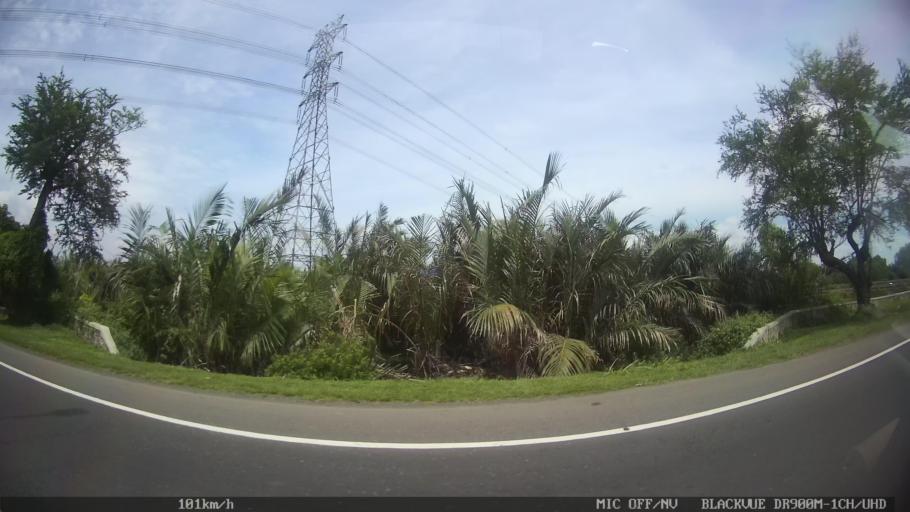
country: ID
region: North Sumatra
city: Labuhan Deli
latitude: 3.7479
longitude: 98.6806
